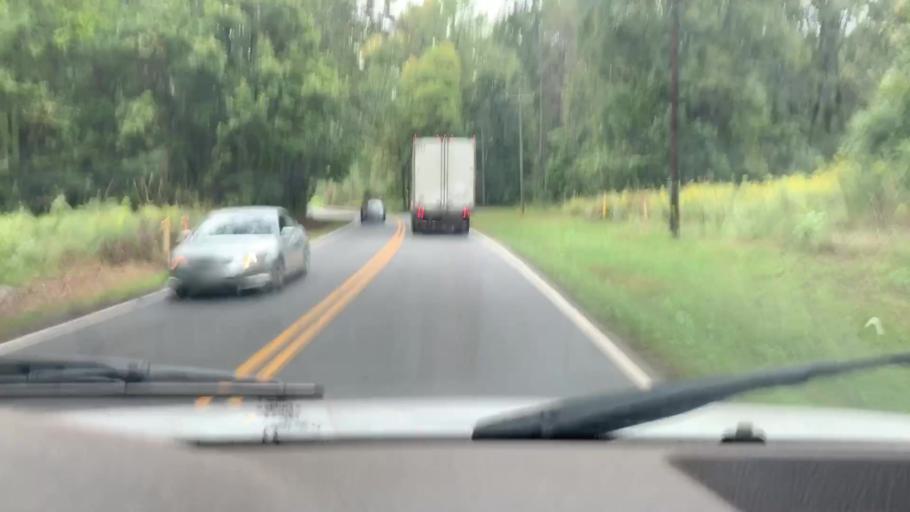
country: US
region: North Carolina
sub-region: Mecklenburg County
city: Huntersville
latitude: 35.3605
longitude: -80.8234
